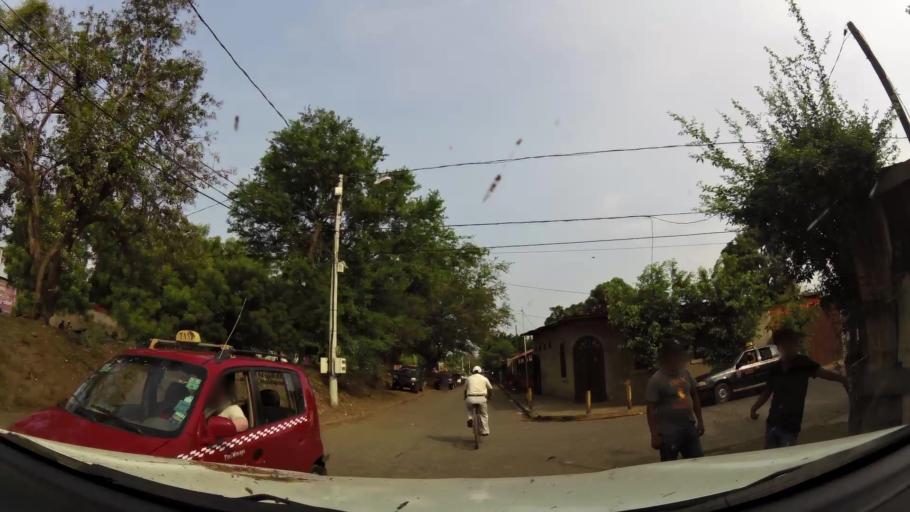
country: NI
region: Masaya
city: Masaya
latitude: 11.9714
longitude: -86.0872
